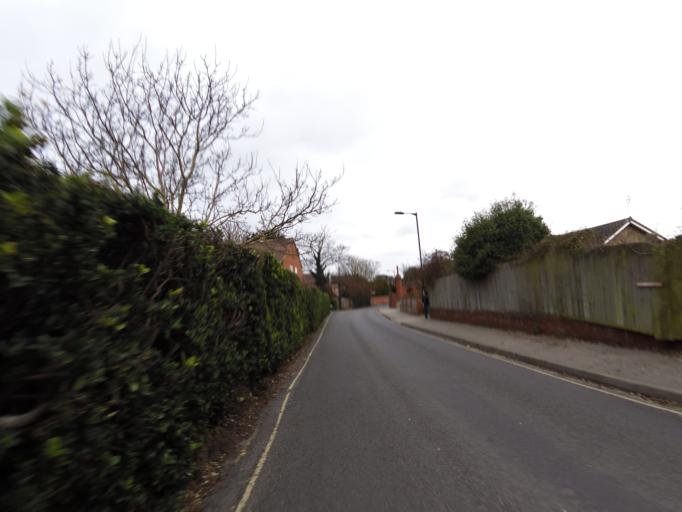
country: GB
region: England
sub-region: Suffolk
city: Felixstowe
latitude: 51.9664
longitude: 1.3684
